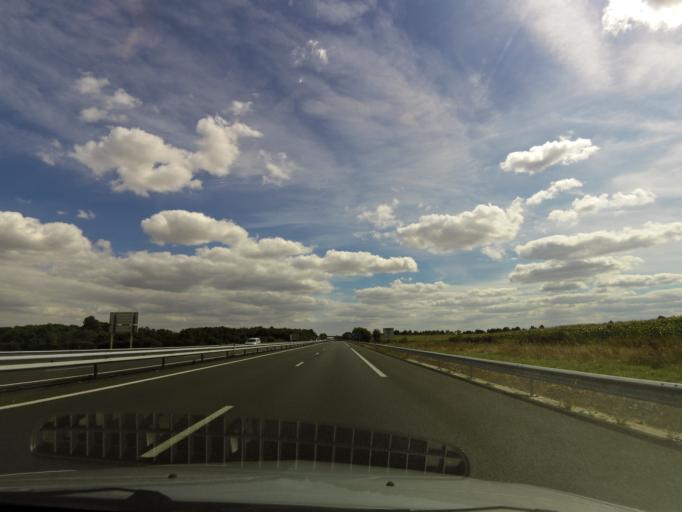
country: FR
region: Pays de la Loire
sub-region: Departement de la Vendee
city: Les Essarts
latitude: 46.8219
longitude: -1.2188
